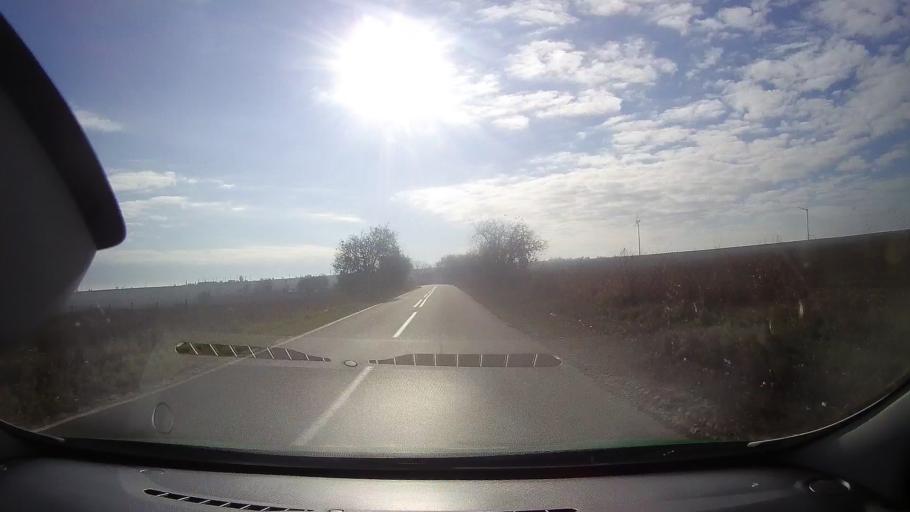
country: RO
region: Tulcea
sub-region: Comuna Mahmudia
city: Mahmudia
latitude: 45.0763
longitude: 29.0801
